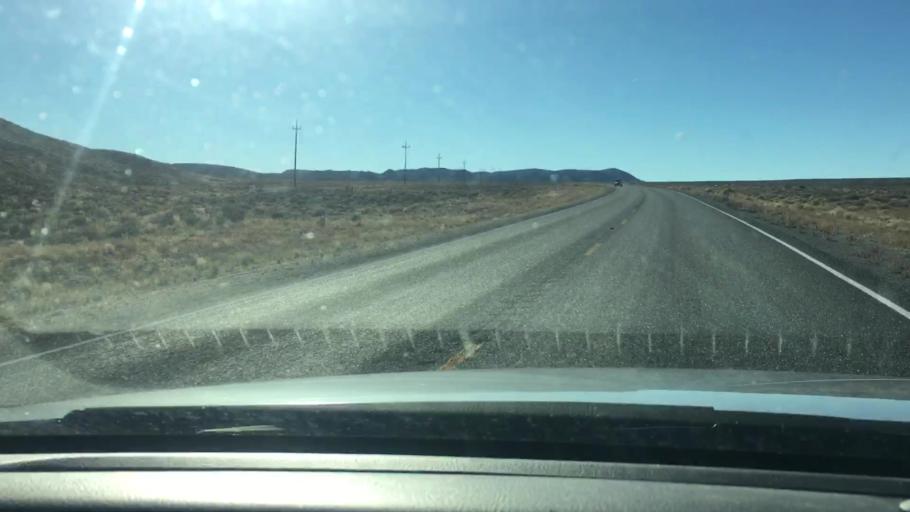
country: US
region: Nevada
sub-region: Nye County
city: Tonopah
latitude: 38.1267
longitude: -116.8473
